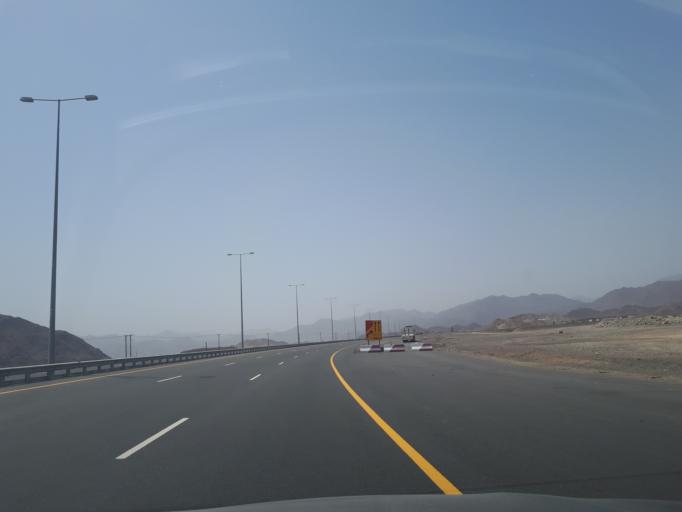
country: OM
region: Muhafazat ad Dakhiliyah
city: Sufalat Sama'il
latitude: 23.3061
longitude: 58.1106
